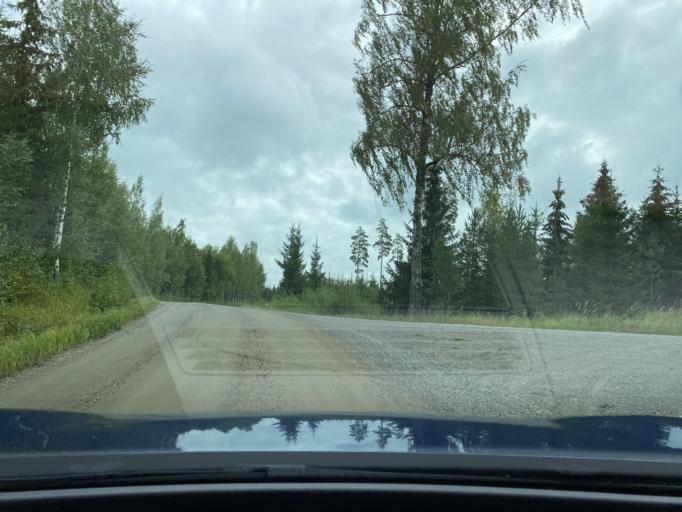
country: FI
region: Pirkanmaa
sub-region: Lounais-Pirkanmaa
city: Punkalaidun
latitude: 61.2117
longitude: 23.1697
